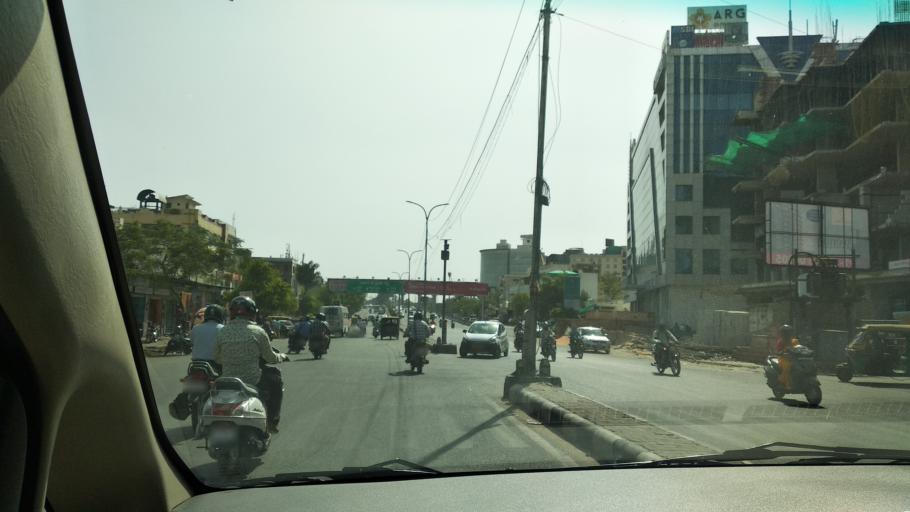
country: IN
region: Rajasthan
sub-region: Jaipur
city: Jaipur
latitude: 26.9147
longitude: 75.7947
